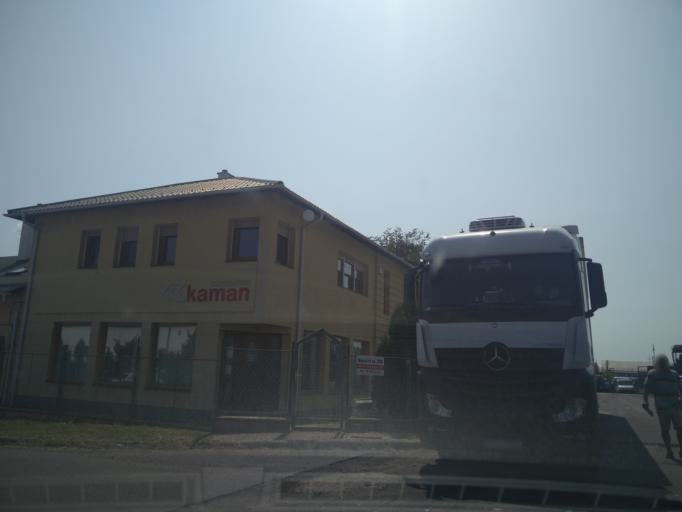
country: HU
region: Zala
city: Zalaegerszeg
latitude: 46.8393
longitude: 16.8628
